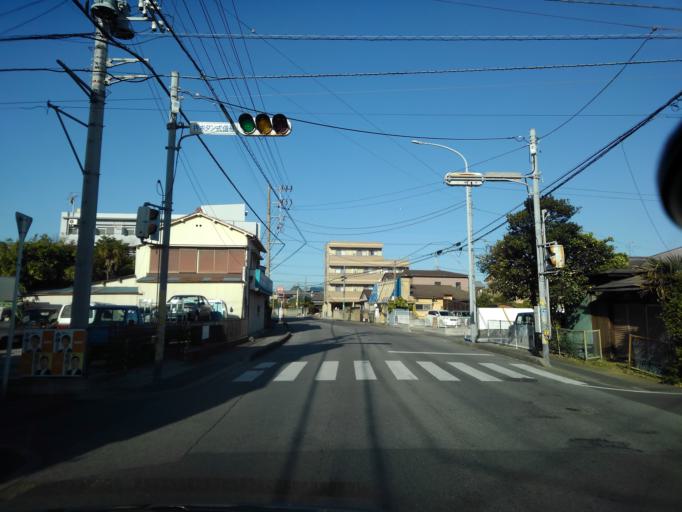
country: JP
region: Chiba
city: Funabashi
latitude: 35.6601
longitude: 140.0520
